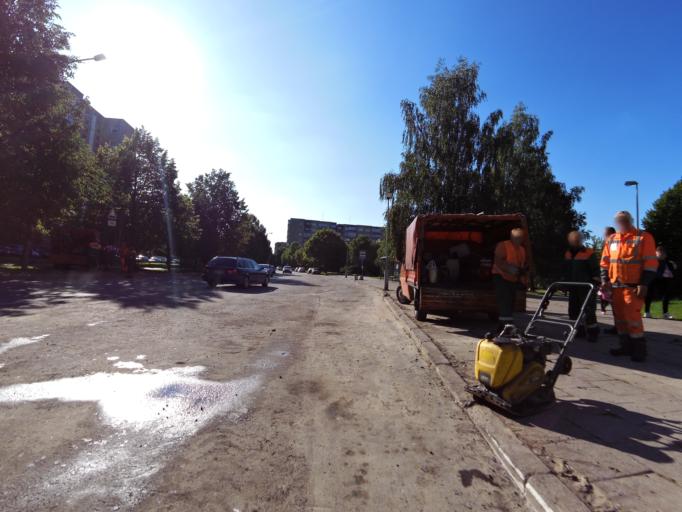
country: LT
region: Vilnius County
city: Justiniskes
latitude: 54.7215
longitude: 25.2177
